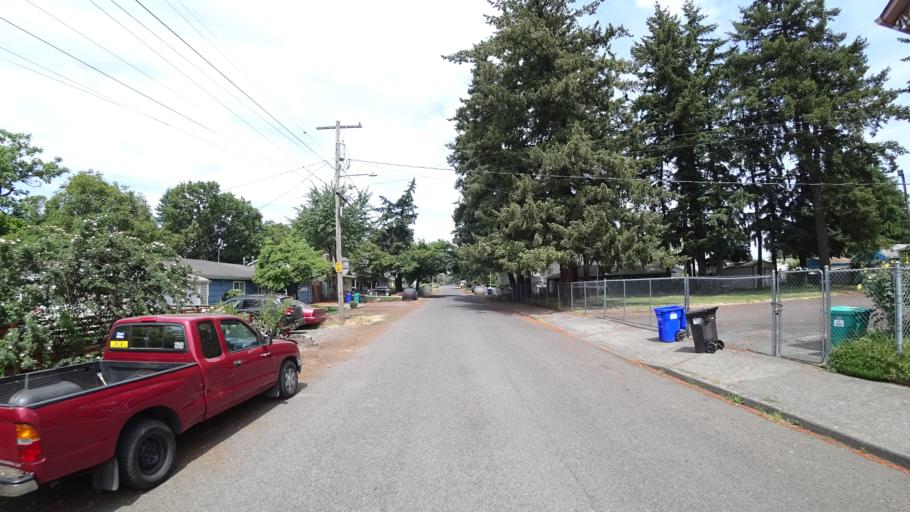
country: US
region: Oregon
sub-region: Multnomah County
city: Lents
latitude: 45.4690
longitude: -122.5923
